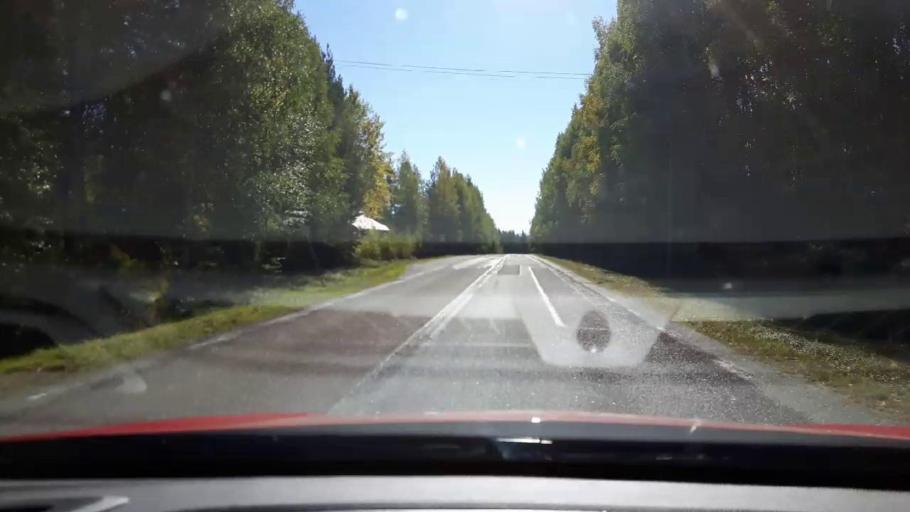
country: SE
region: Jaemtland
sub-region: Harjedalens Kommun
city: Sveg
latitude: 62.1251
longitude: 14.1639
